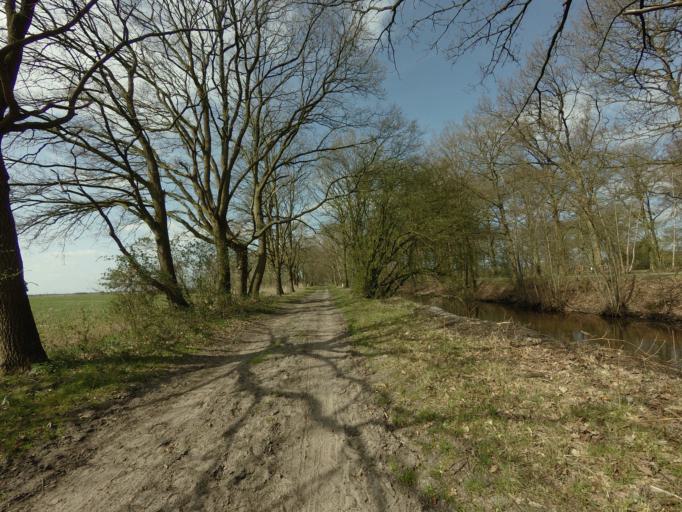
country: NL
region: North Holland
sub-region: Gemeente Wijdemeren
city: Nieuw-Loosdrecht
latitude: 52.1792
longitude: 5.1583
